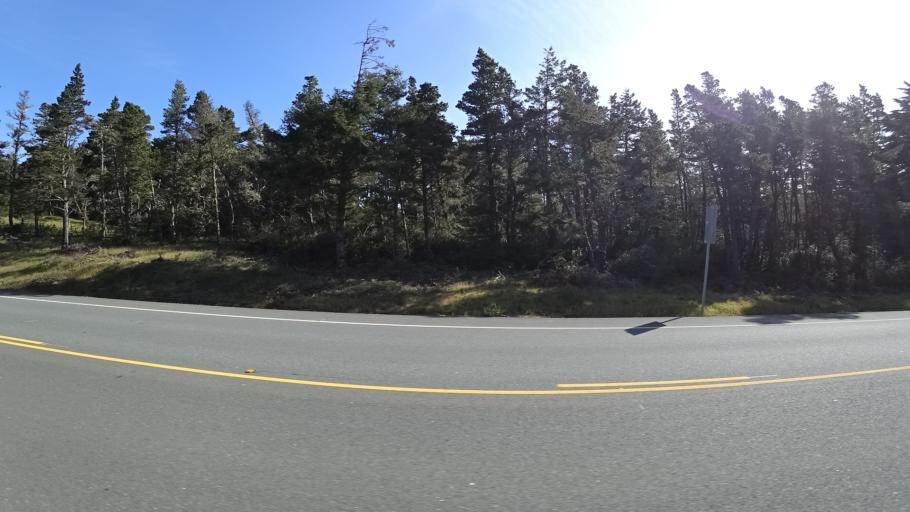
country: US
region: Oregon
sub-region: Curry County
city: Gold Beach
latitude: 42.2515
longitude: -124.3938
